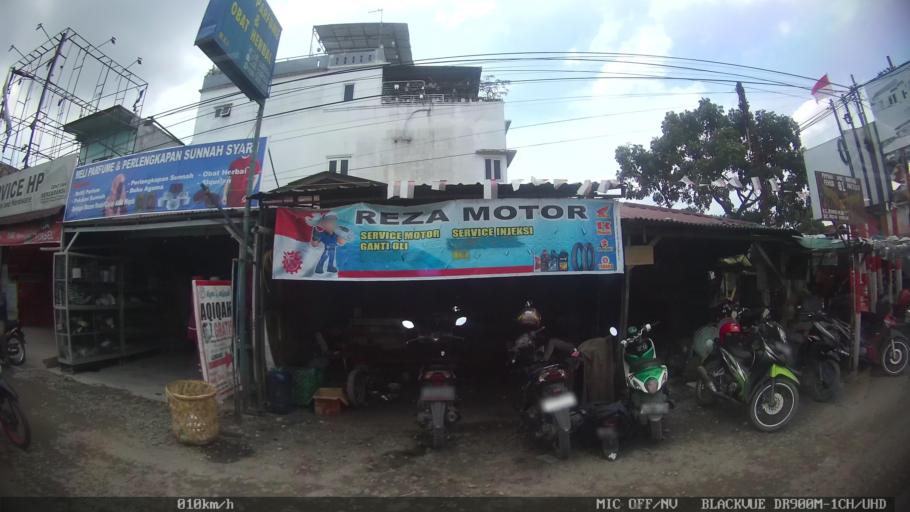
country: ID
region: North Sumatra
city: Labuhan Deli
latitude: 3.6968
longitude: 98.6566
